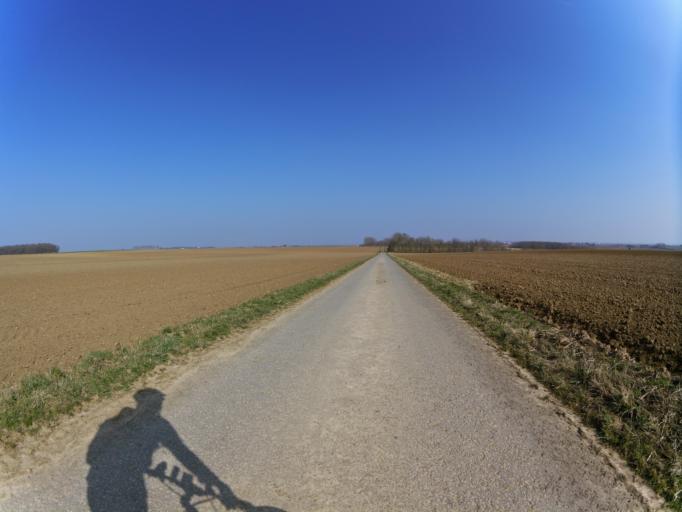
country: DE
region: Bavaria
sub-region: Regierungsbezirk Unterfranken
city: Sulzdorf
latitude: 49.6601
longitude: 9.9064
